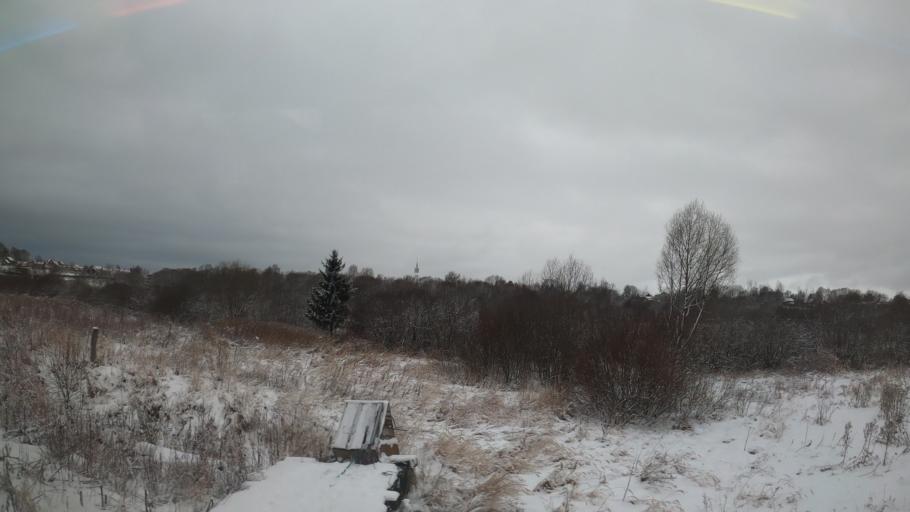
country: RU
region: Jaroslavl
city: Pereslavl'-Zalesskiy
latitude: 56.7049
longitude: 38.9095
